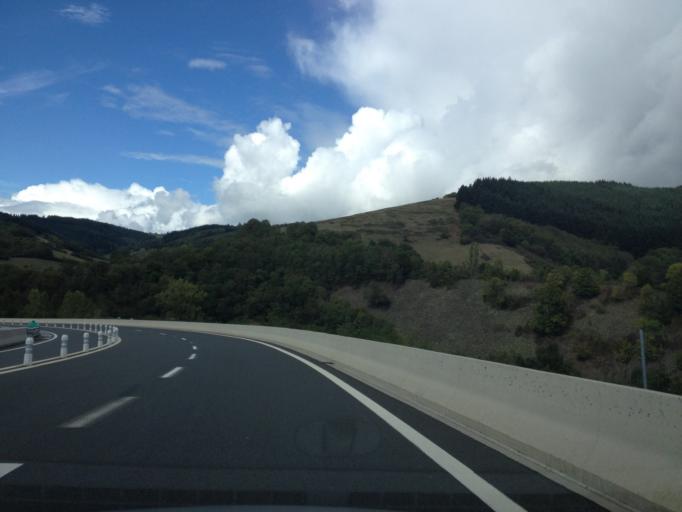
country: FR
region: Rhone-Alpes
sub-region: Departement du Rhone
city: Tarare
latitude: 45.8902
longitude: 4.4078
